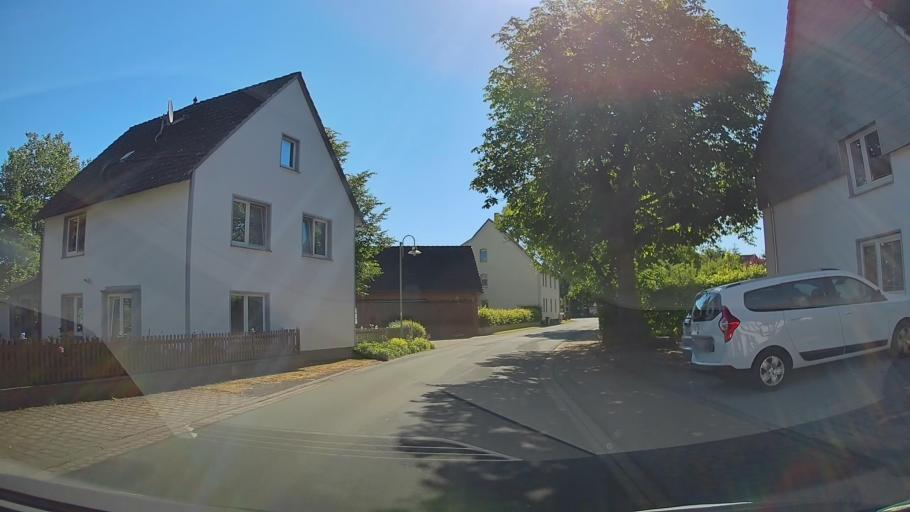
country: DE
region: Lower Saxony
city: Vahlbruch
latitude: 51.9687
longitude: 9.3556
